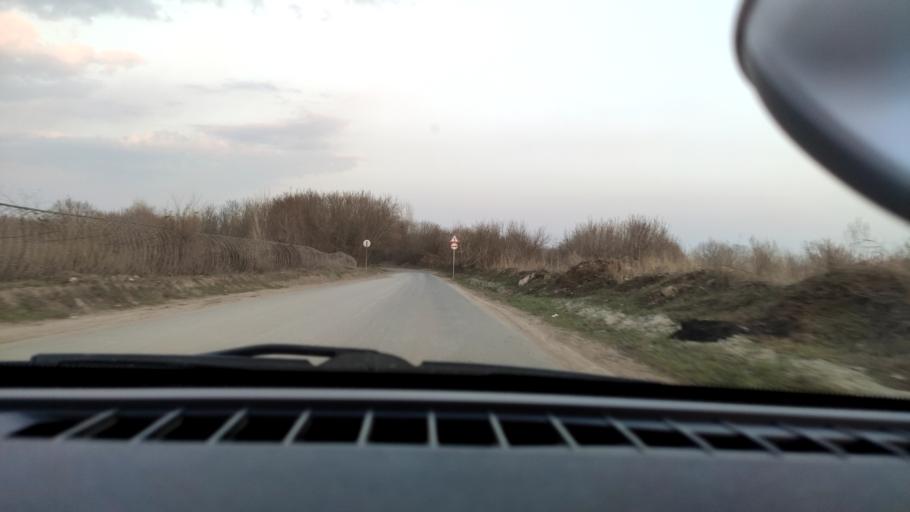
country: RU
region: Samara
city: Smyshlyayevka
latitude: 53.2064
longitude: 50.3132
